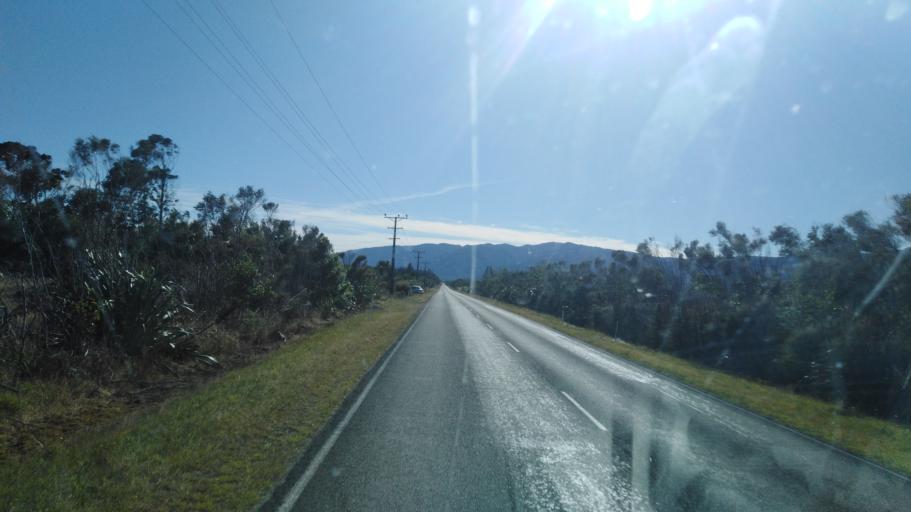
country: NZ
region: West Coast
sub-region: Buller District
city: Westport
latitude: -41.7486
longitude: 171.6774
